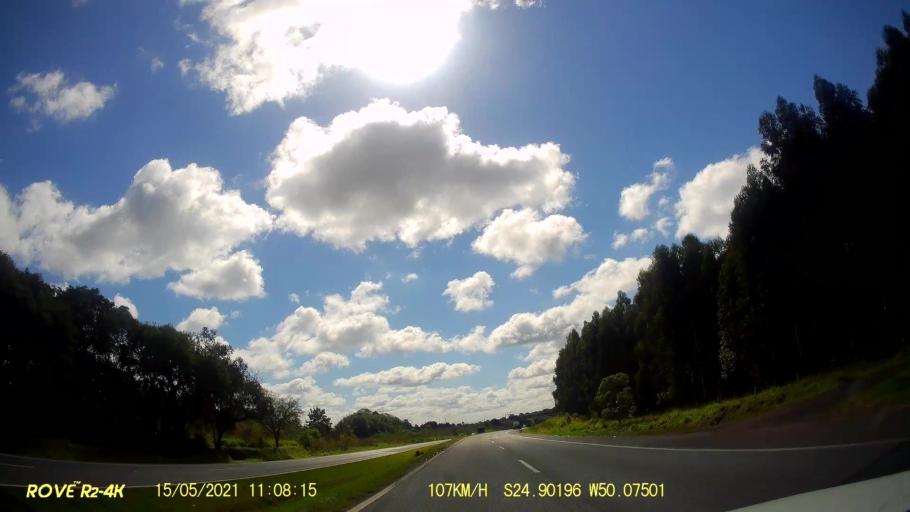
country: BR
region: Parana
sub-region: Carambei
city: Carambei
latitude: -24.9021
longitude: -50.0751
